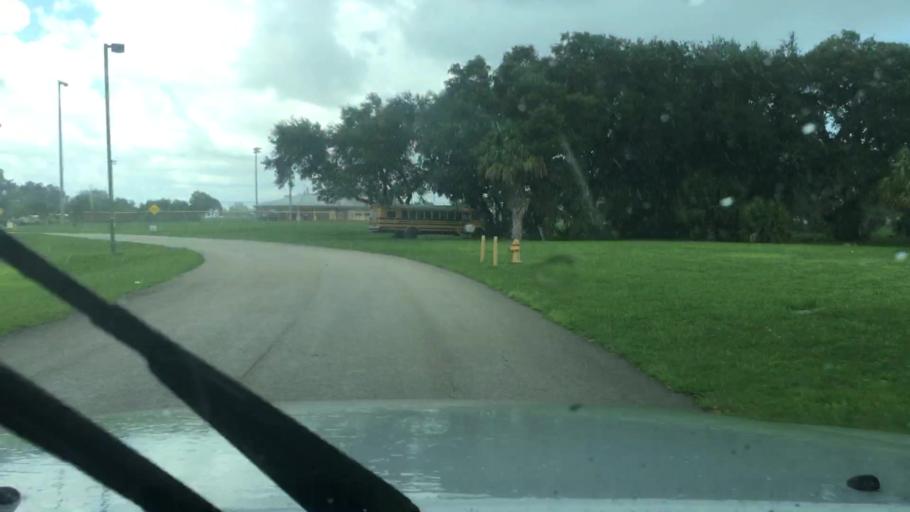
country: US
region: Florida
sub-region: Miami-Dade County
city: Ives Estates
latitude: 25.9696
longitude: -80.1688
